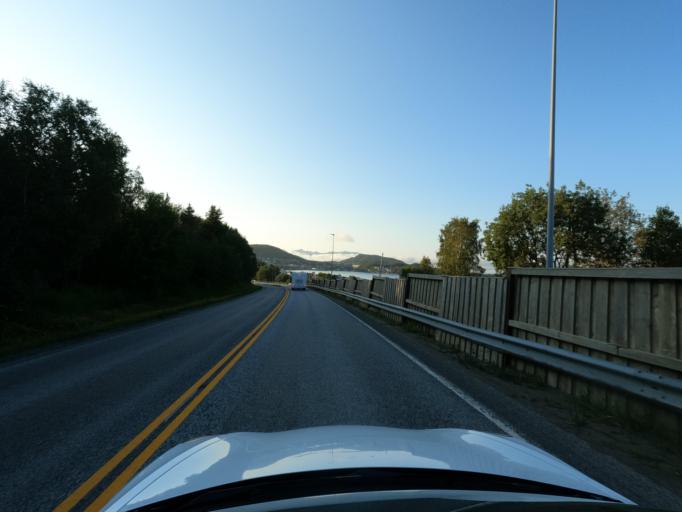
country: NO
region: Troms
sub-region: Harstad
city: Harstad
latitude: 68.7584
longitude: 16.5681
